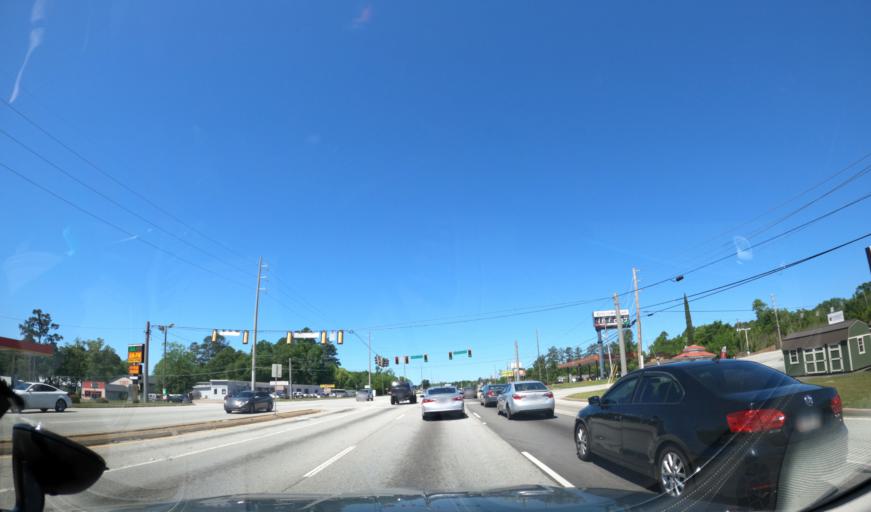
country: US
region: Georgia
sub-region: Columbia County
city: Martinez
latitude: 33.4519
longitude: -82.0457
